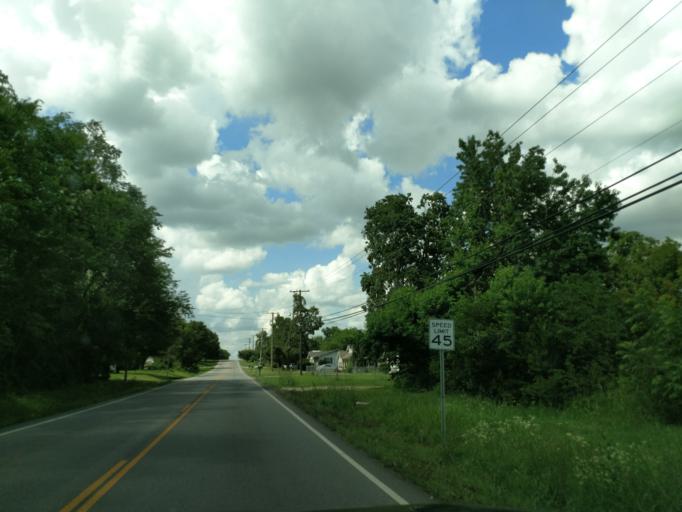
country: US
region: Arkansas
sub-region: Carroll County
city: Berryville
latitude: 36.3743
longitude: -93.5673
